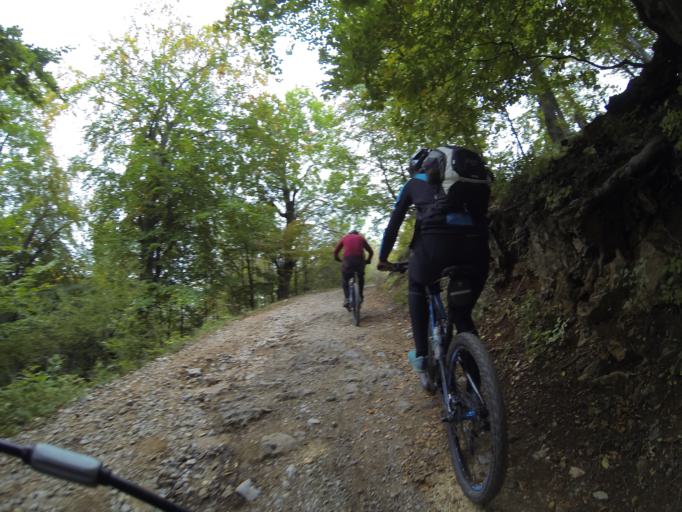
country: RO
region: Gorj
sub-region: Comuna Tismana
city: Sohodol
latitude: 45.0681
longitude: 22.8646
